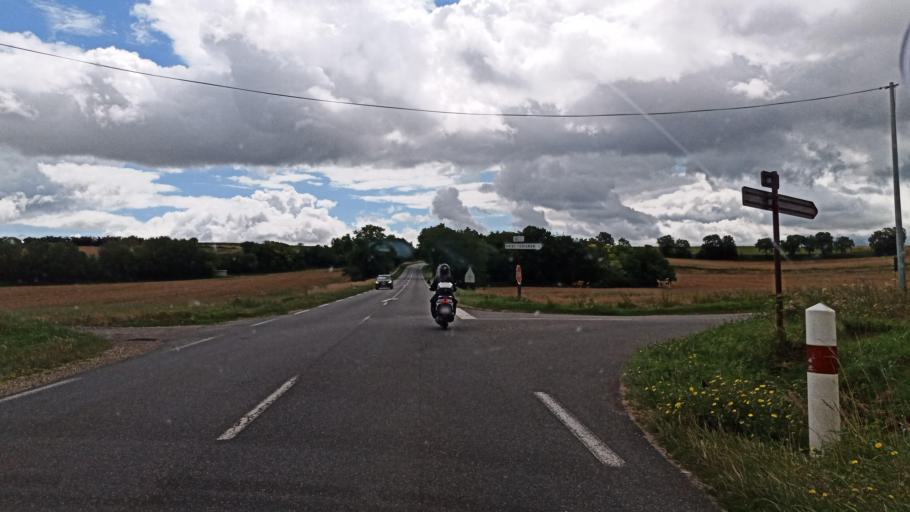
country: FR
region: Ile-de-France
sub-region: Departement de Seine-et-Marne
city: Cannes-Ecluse
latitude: 48.3373
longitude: 2.9580
